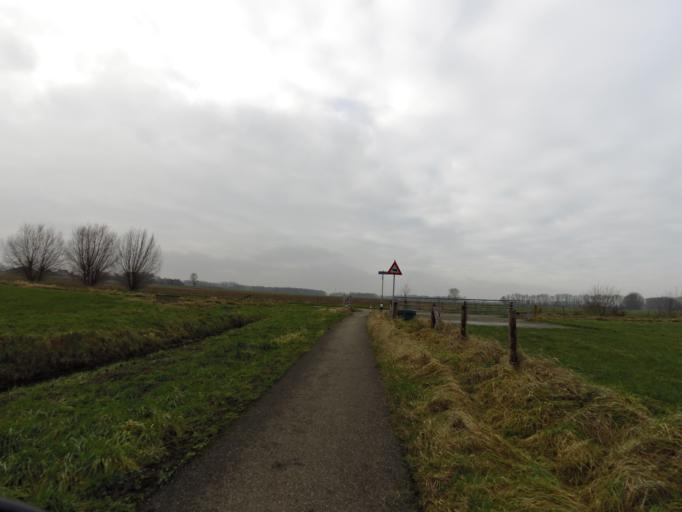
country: NL
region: Gelderland
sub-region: Gemeente Doesburg
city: Doesburg
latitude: 51.9912
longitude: 6.1825
